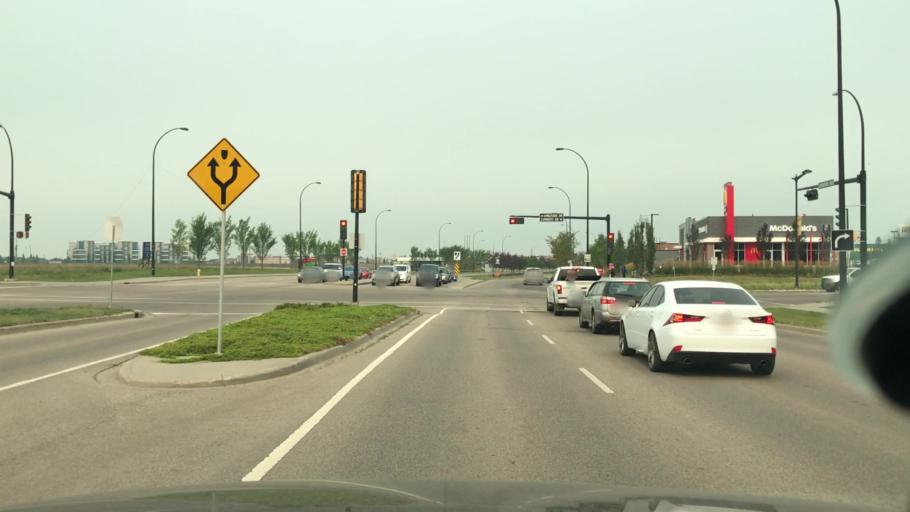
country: CA
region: Alberta
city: Devon
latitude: 53.4351
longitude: -113.6072
